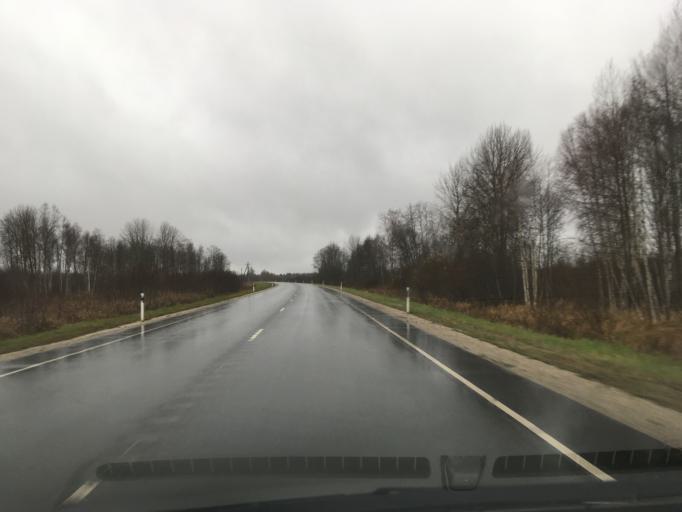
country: EE
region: Laeaene
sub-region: Lihula vald
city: Lihula
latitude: 58.8436
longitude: 24.0606
